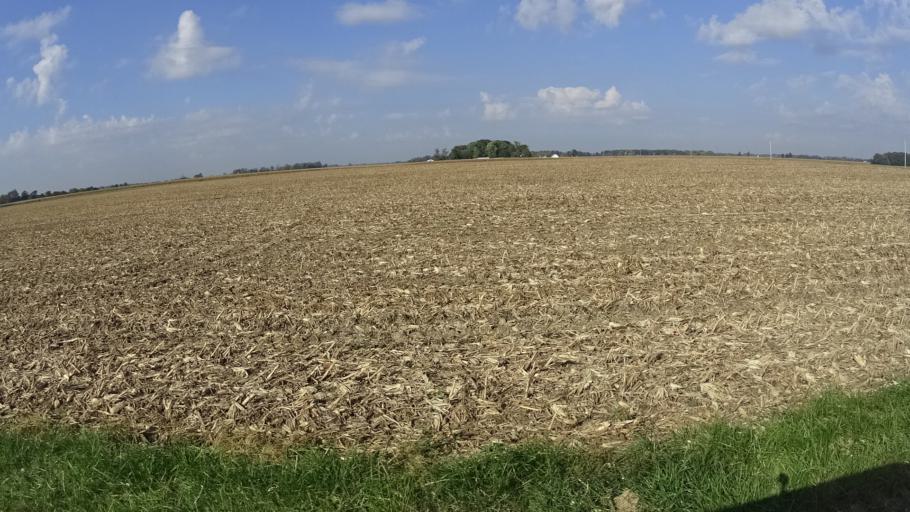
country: US
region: Indiana
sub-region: Madison County
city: Lapel
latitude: 40.0443
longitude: -85.8626
